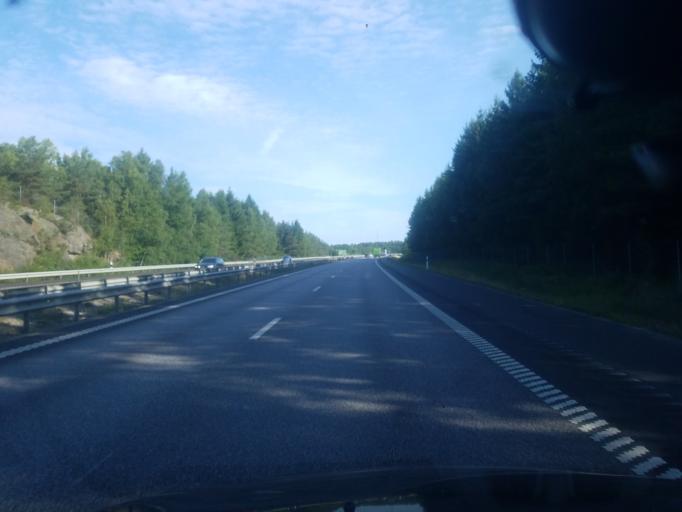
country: SE
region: Vaestra Goetaland
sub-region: Stenungsunds Kommun
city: Stora Hoga
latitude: 57.9923
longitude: 11.8424
